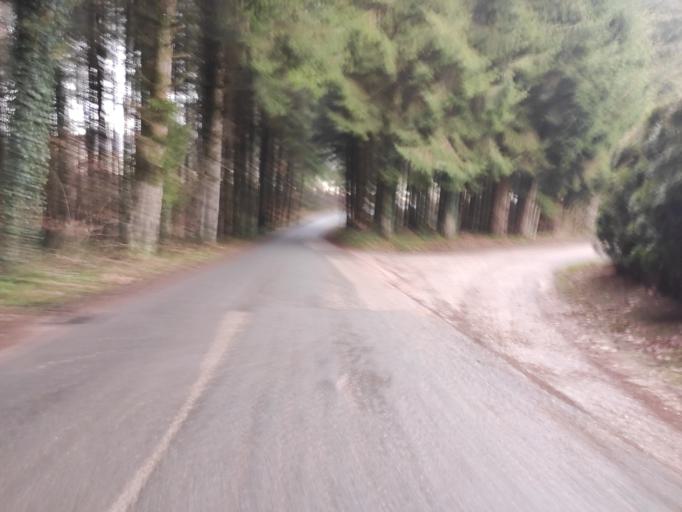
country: AT
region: Salzburg
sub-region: Politischer Bezirk Salzburg-Umgebung
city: Obertrum am See
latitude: 47.9141
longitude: 13.0693
